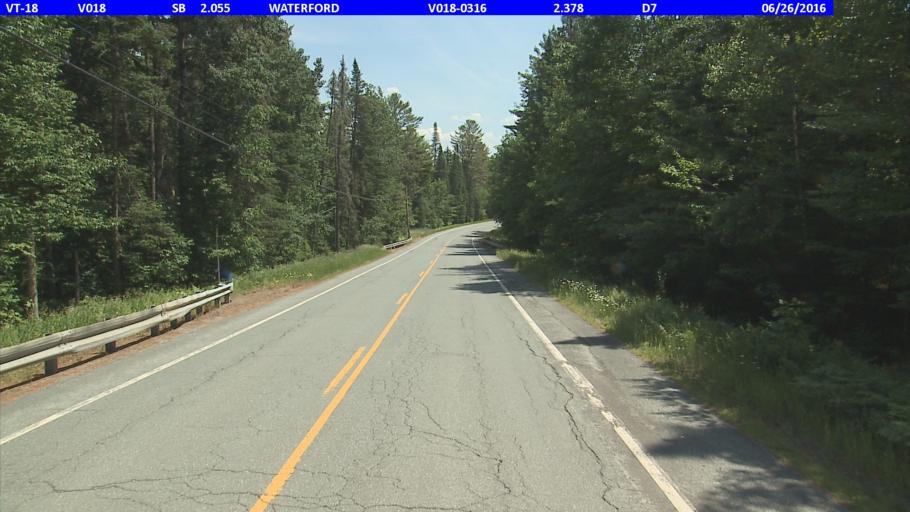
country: US
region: Vermont
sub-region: Caledonia County
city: Saint Johnsbury
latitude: 44.3664
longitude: -71.9056
